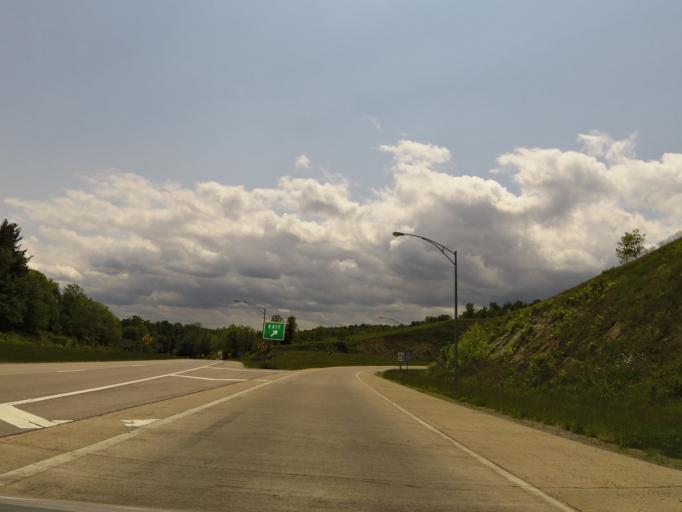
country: US
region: Ohio
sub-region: Meigs County
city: Pomeroy
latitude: 39.0547
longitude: -82.0165
